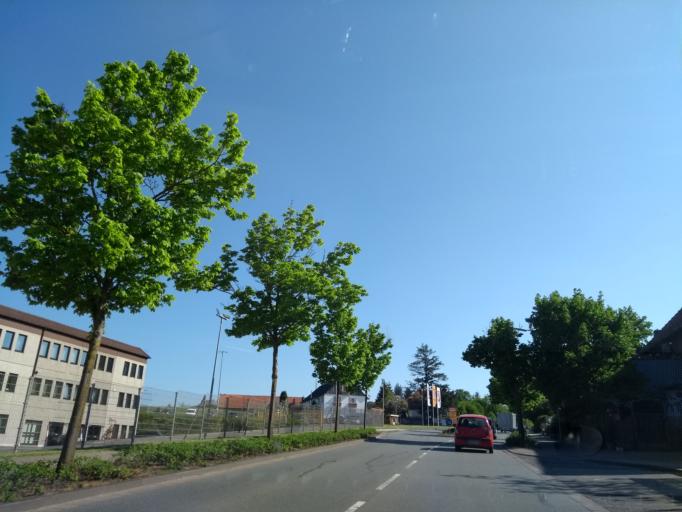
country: DE
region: Hesse
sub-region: Regierungsbezirk Kassel
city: Korbach
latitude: 51.3080
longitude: 8.9059
